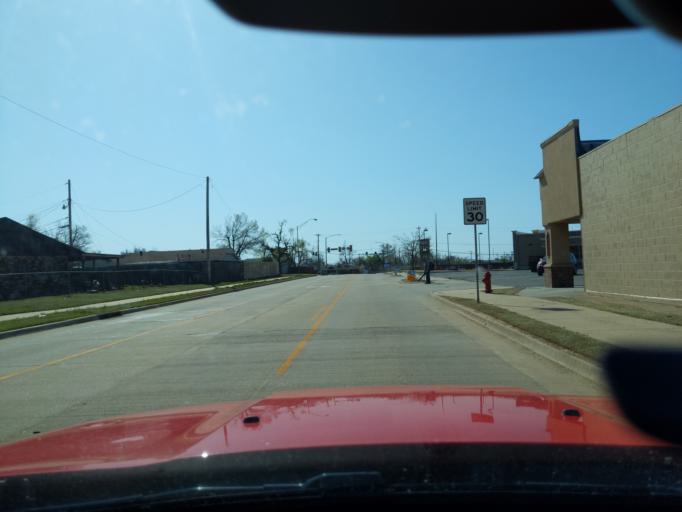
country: US
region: Oklahoma
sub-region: Cleveland County
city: Moore
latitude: 35.3446
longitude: -97.4878
